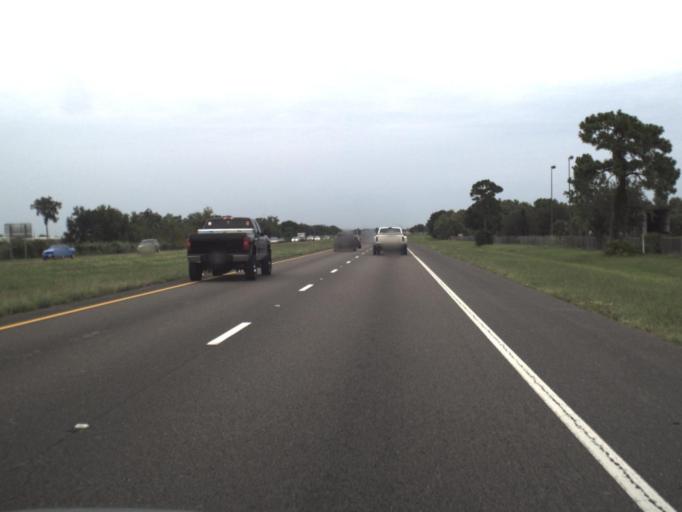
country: US
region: Florida
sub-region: Manatee County
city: Whitfield
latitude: 27.4051
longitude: -82.5328
